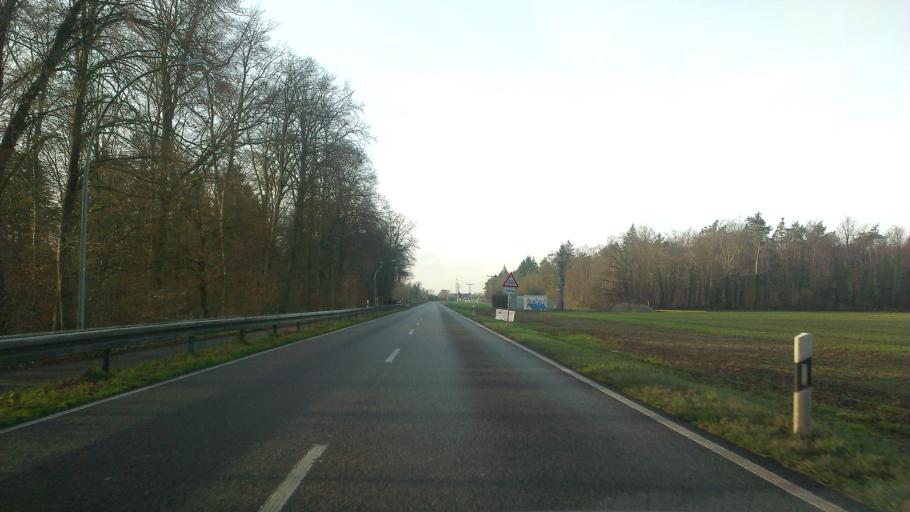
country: DE
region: Baden-Wuerttemberg
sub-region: Karlsruhe Region
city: Waghausel
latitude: 49.2479
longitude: 8.5279
